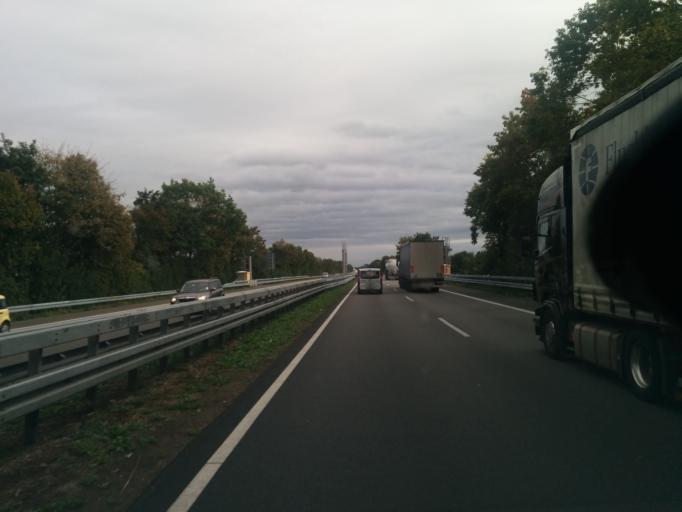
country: DE
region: North Rhine-Westphalia
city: Meckenheim
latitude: 50.6095
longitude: 6.9933
